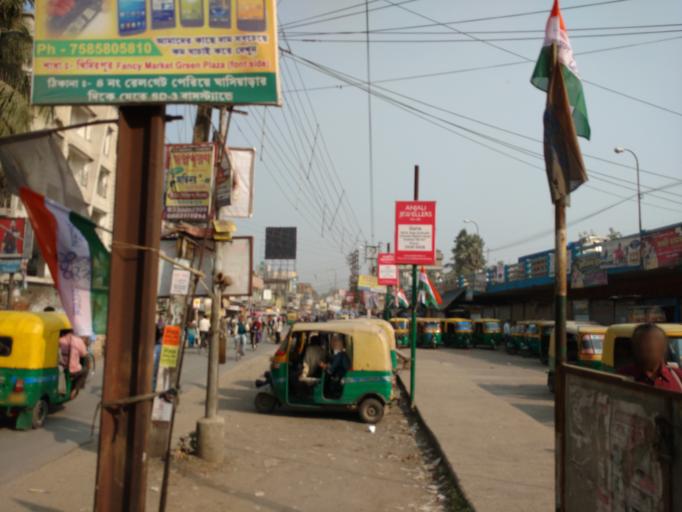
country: IN
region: West Bengal
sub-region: South 24 Paraganas
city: Champahati
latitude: 22.4418
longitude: 88.4336
